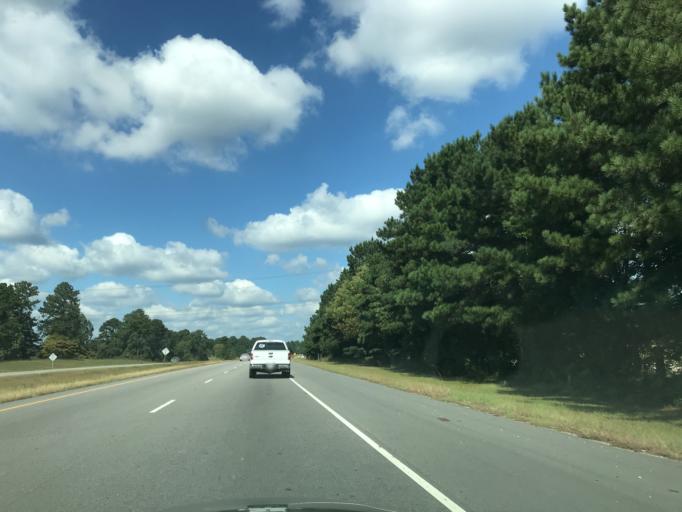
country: US
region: North Carolina
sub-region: Wake County
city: Wake Forest
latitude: 35.9330
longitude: -78.5429
